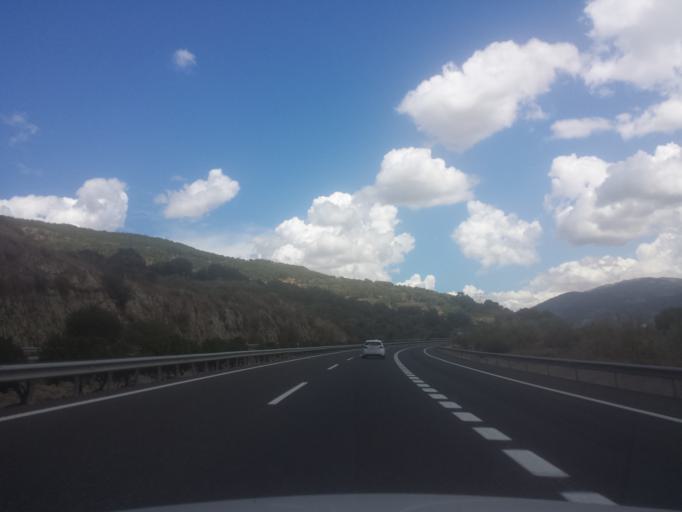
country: ES
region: Extremadura
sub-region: Provincia de Caceres
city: Hervas
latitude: 40.2911
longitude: -5.8985
